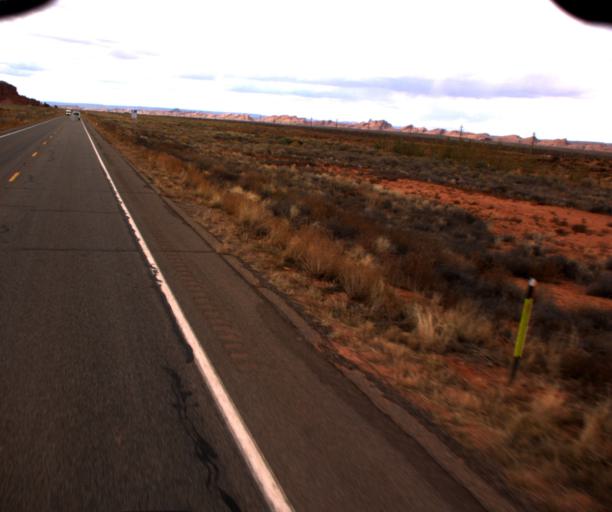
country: US
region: Arizona
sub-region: Navajo County
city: Kayenta
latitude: 36.7812
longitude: -109.9881
